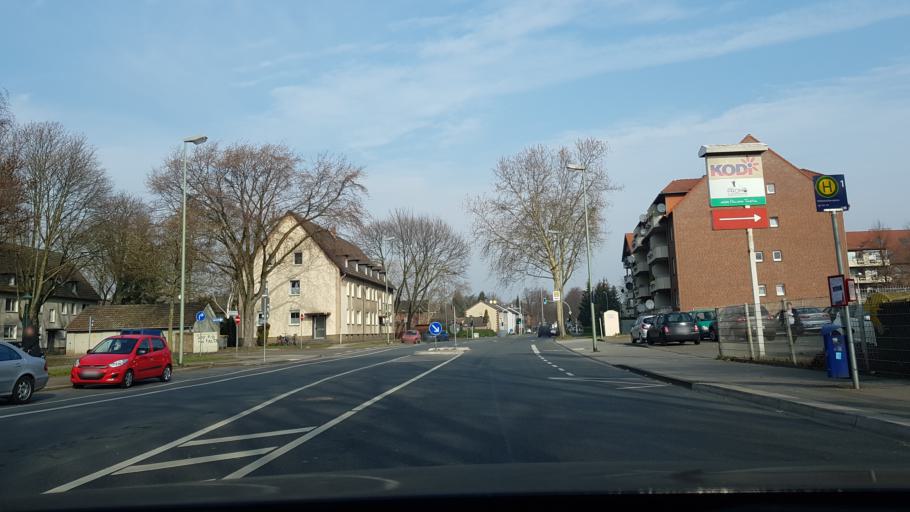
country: DE
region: North Rhine-Westphalia
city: Meiderich
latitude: 51.4968
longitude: 6.7981
